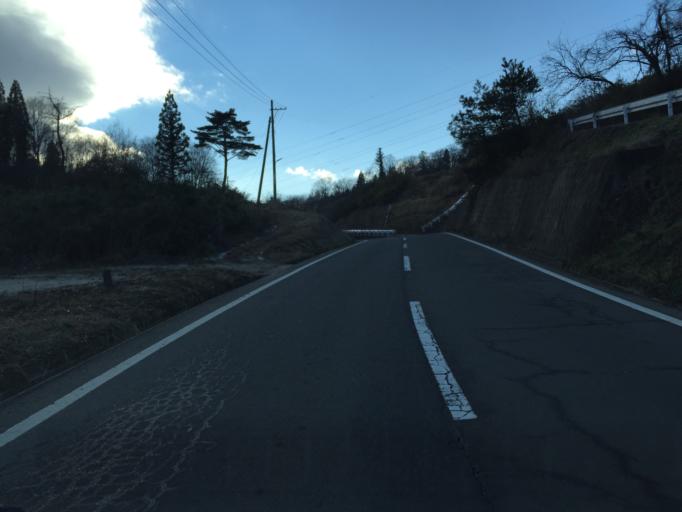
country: JP
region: Fukushima
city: Fukushima-shi
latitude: 37.7121
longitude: 140.4156
